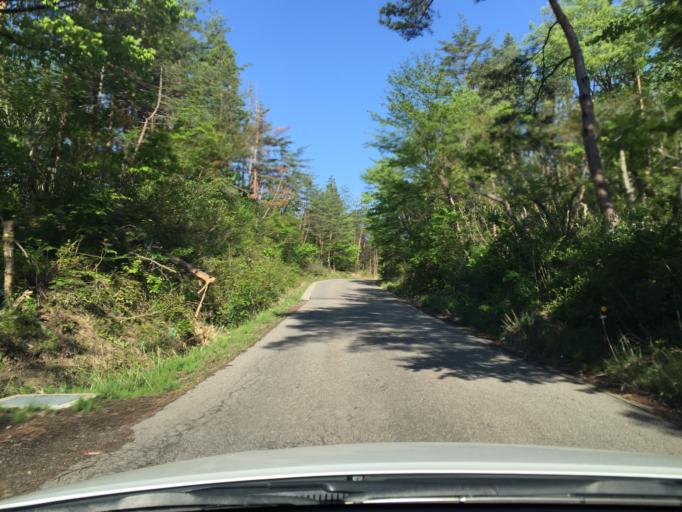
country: JP
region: Fukushima
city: Kitakata
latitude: 37.6691
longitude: 139.8378
